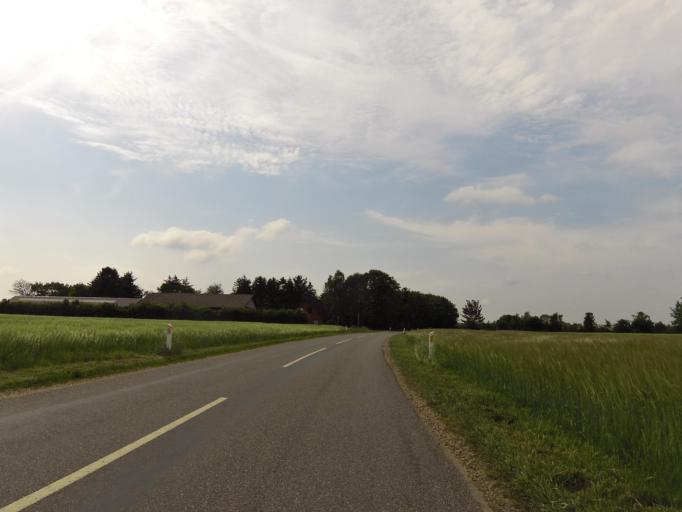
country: DK
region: South Denmark
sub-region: Haderslev Kommune
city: Gram
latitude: 55.2783
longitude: 9.1009
